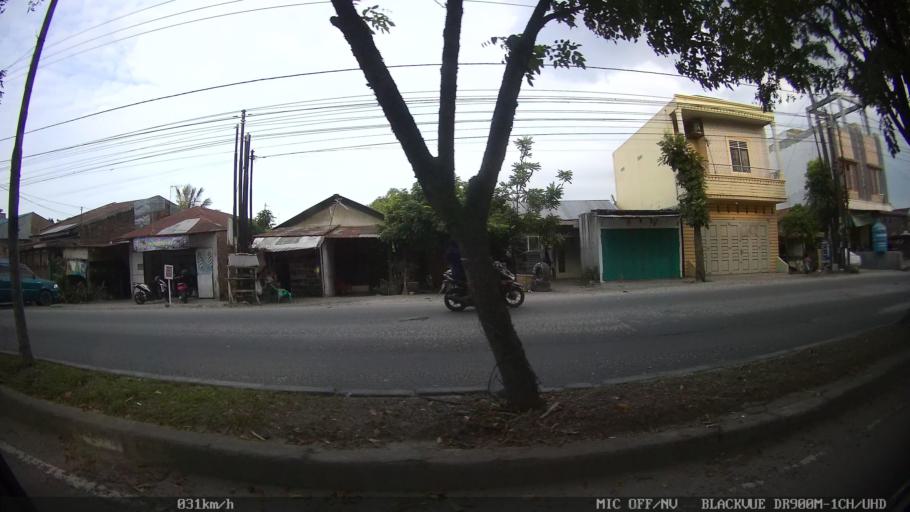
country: ID
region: North Sumatra
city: Sunggal
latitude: 3.5578
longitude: 98.6169
